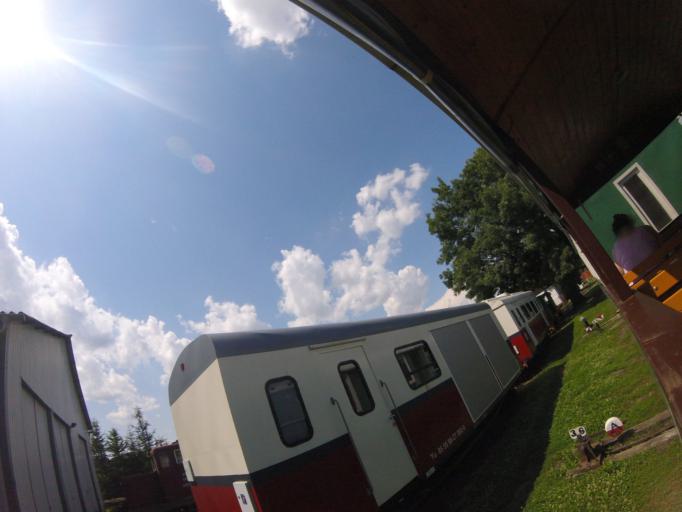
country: HU
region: Zala
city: Lenti
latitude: 46.6062
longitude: 16.6415
